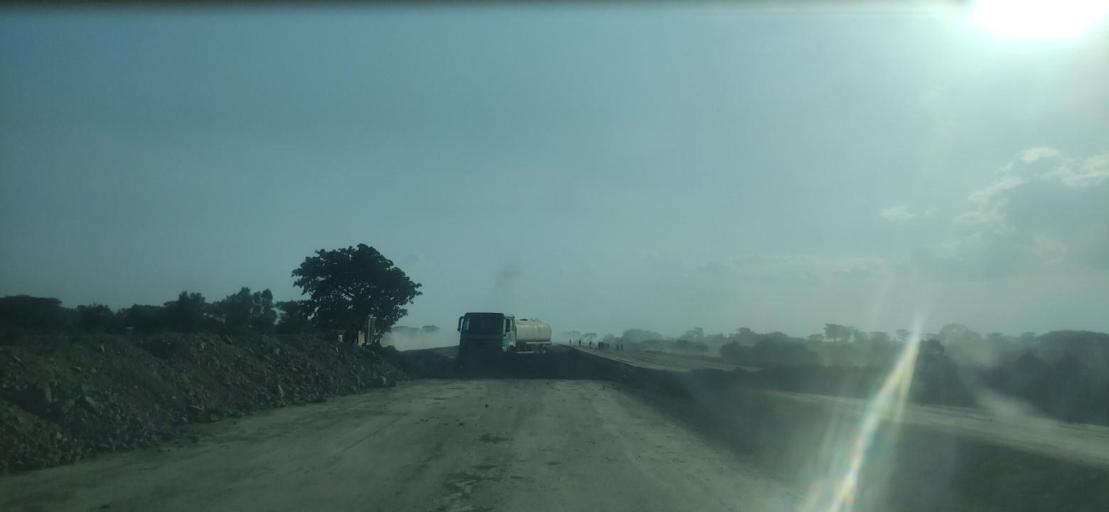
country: ET
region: Southern Nations, Nationalities, and People's Region
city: Hawassa
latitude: 7.1575
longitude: 38.4811
